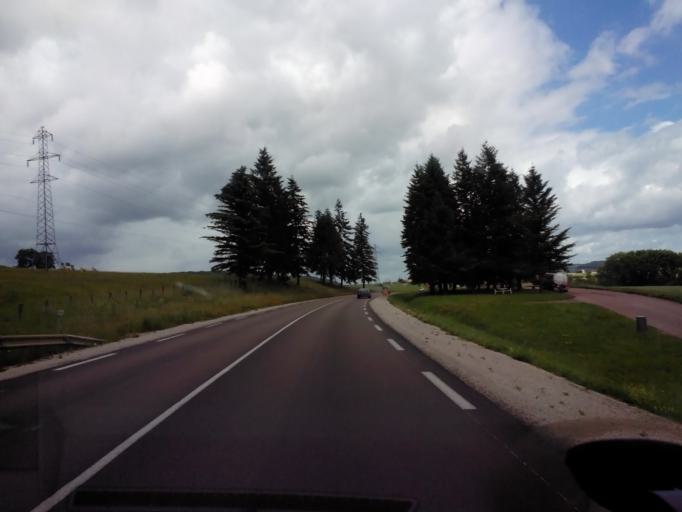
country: FR
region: Champagne-Ardenne
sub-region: Departement de la Haute-Marne
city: Rolampont
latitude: 47.9139
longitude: 5.2896
